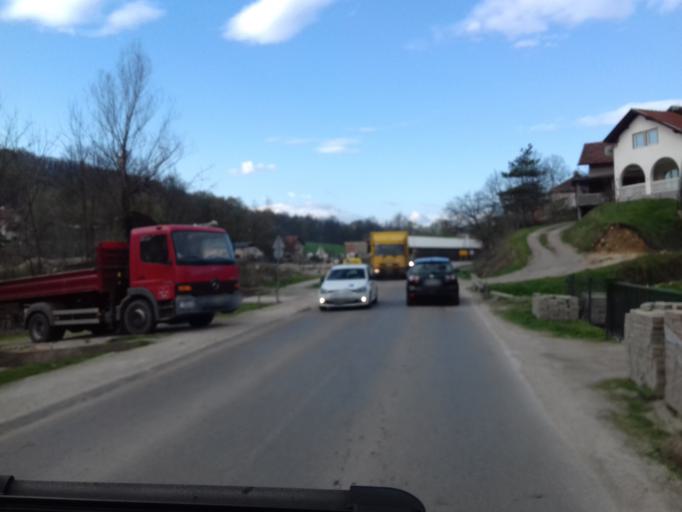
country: BA
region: Federation of Bosnia and Herzegovina
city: Tesanjka
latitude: 44.6373
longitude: 18.0127
